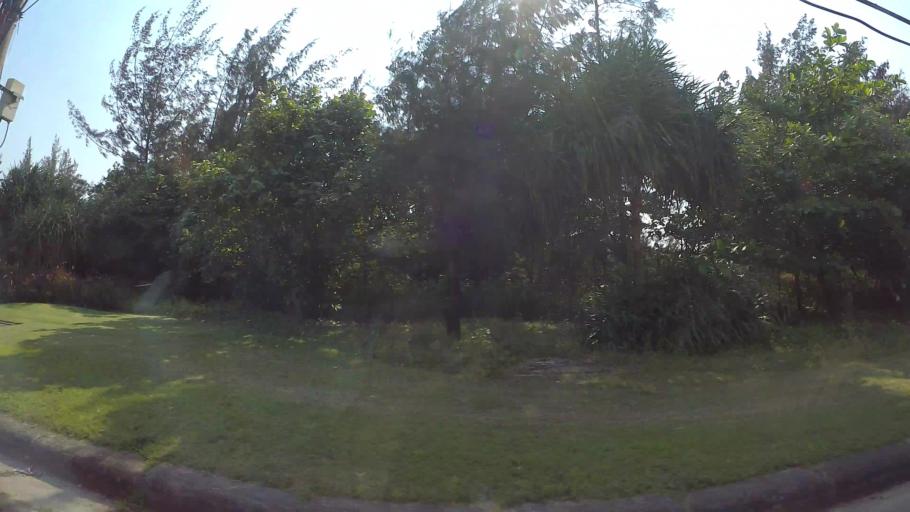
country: VN
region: Da Nang
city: Ngu Hanh Son
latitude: 15.9730
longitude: 108.2806
